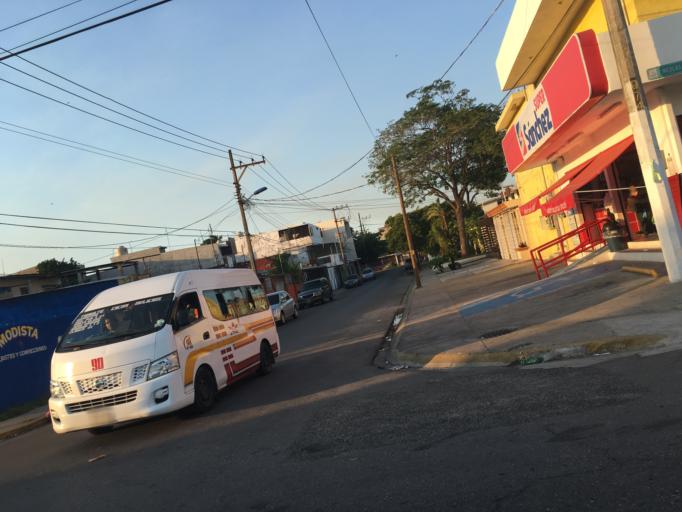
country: MX
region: Tabasco
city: Villahermosa
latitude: 17.9712
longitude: -92.9543
